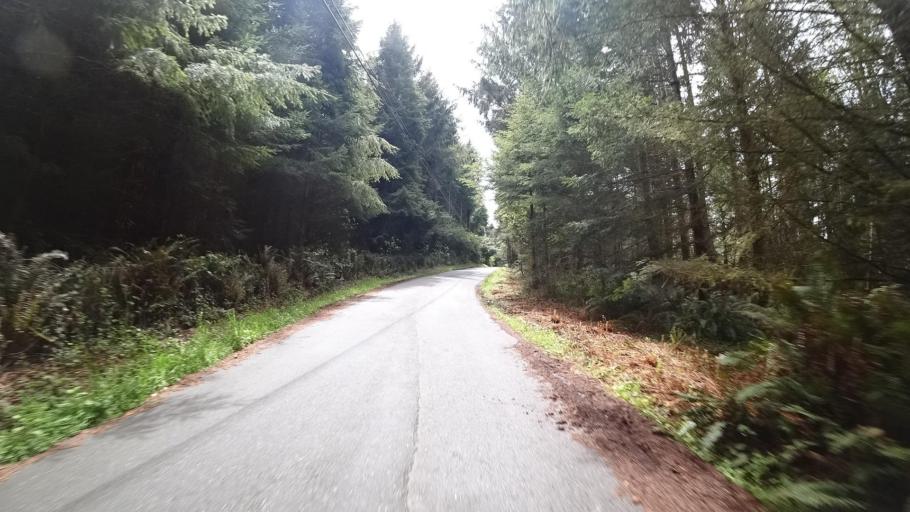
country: US
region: California
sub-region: Humboldt County
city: Bayside
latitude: 40.8331
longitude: -124.0134
